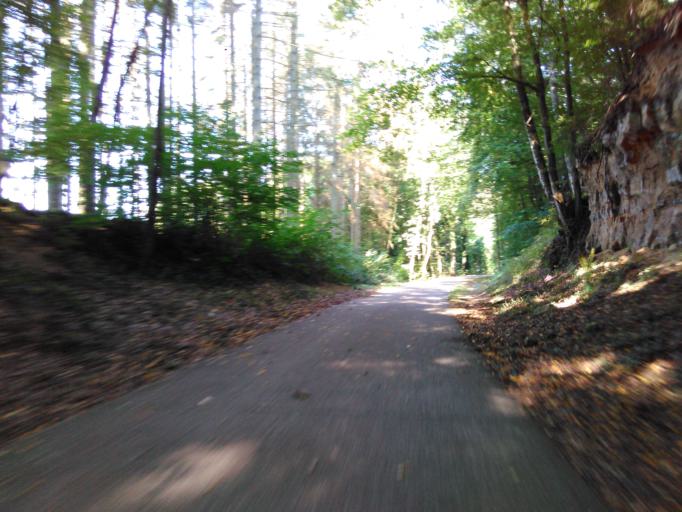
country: LU
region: Luxembourg
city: Eischen
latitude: 49.6714
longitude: 5.8839
